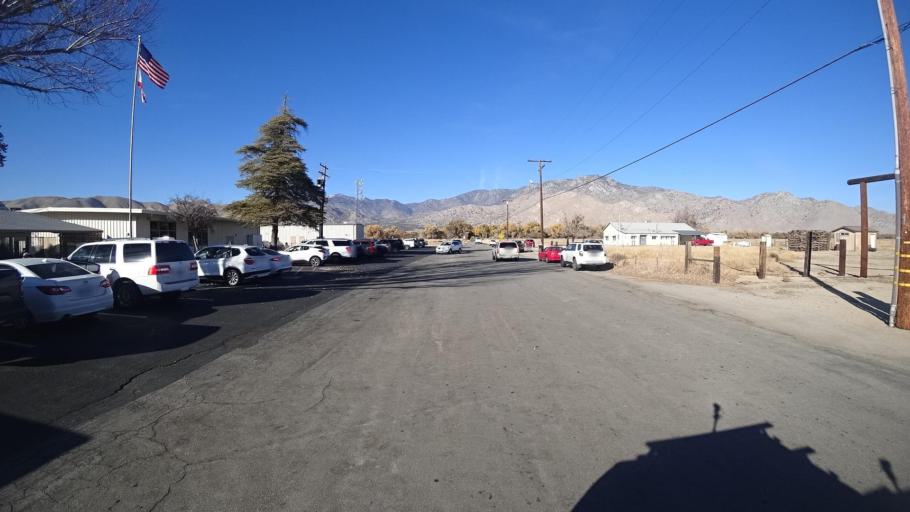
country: US
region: California
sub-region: Kern County
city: Weldon
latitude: 35.6663
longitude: -118.2901
